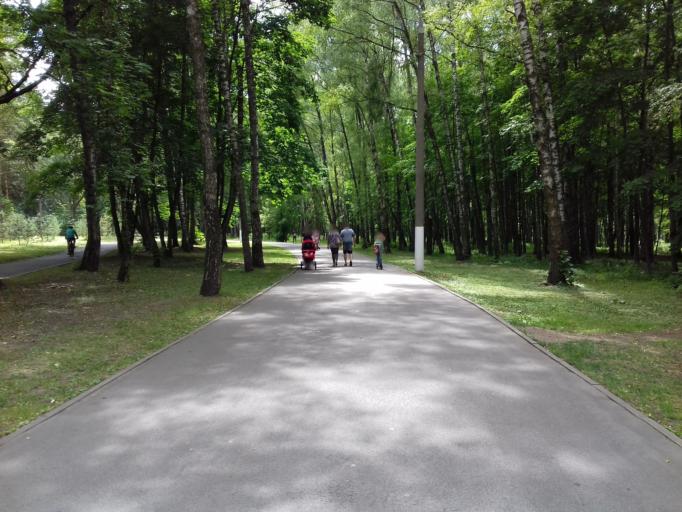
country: RU
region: Tula
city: Tula
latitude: 54.1857
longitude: 37.5849
